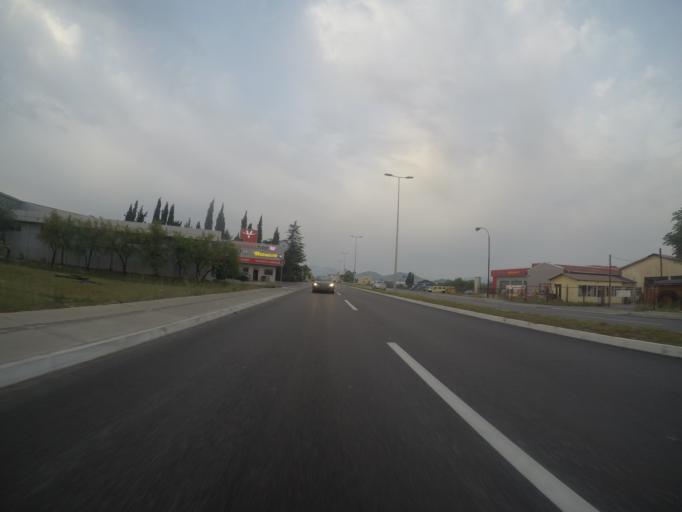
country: ME
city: Mojanovici
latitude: 42.3611
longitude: 19.2251
